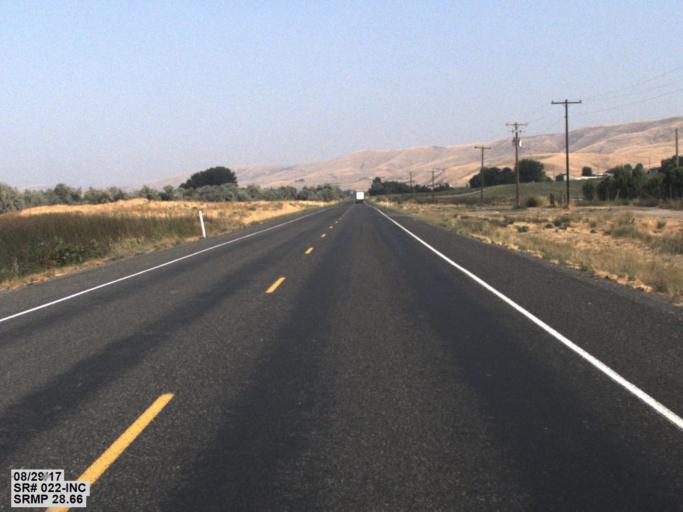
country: US
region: Washington
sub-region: Yakima County
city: Grandview
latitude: 46.1889
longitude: -119.8893
